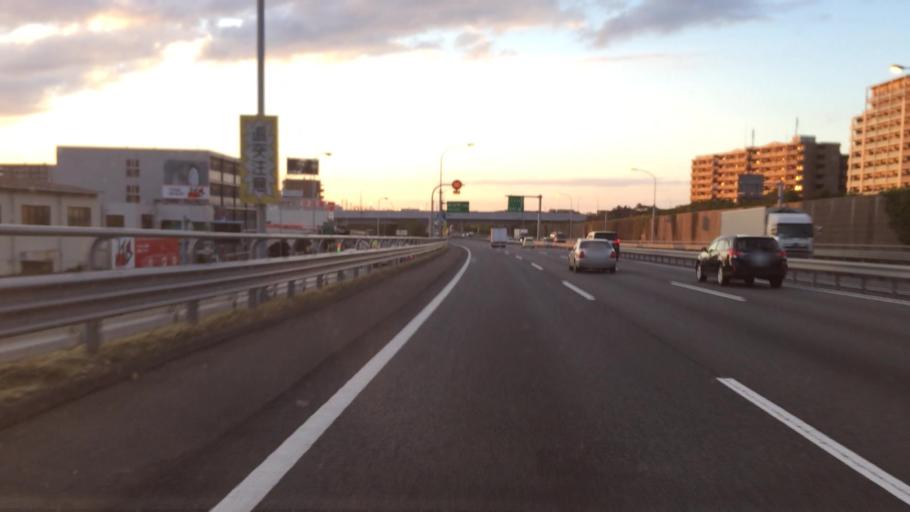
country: JP
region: Chiba
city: Funabashi
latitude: 35.6579
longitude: 140.0366
